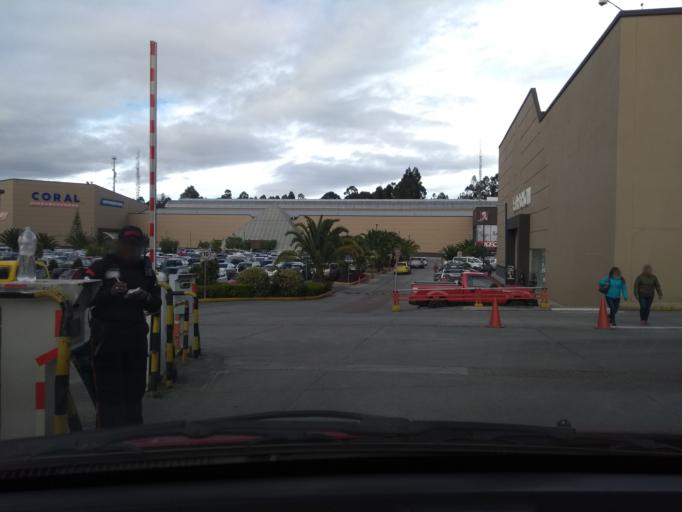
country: EC
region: Azuay
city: Cuenca
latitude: -2.9191
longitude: -79.0164
